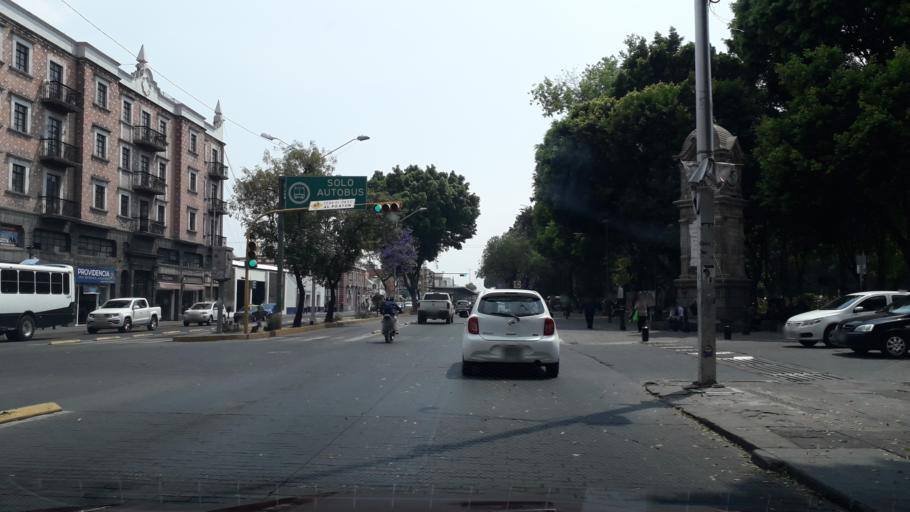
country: MX
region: Puebla
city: Puebla
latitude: 19.0485
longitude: -98.2063
